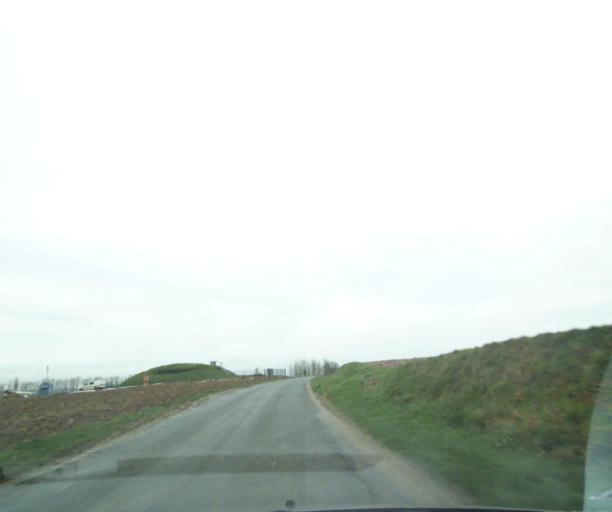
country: FR
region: Picardie
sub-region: Departement de l'Oise
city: Noyon
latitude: 49.5790
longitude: 2.9717
